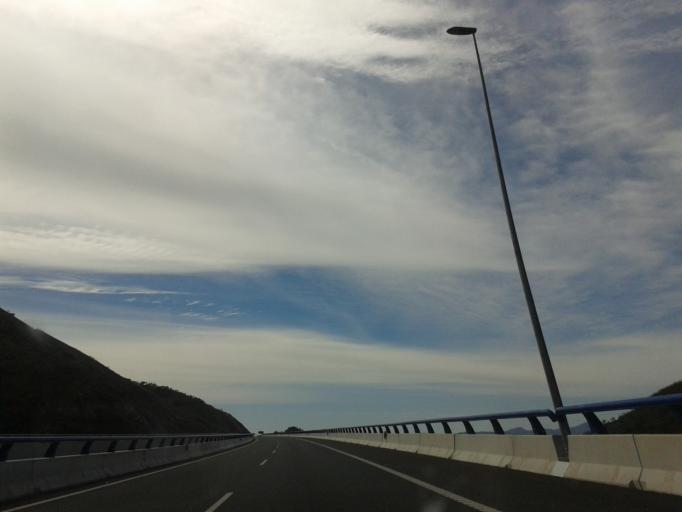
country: ES
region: Andalusia
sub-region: Provincia de Malaga
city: Almogia
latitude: 36.8553
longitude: -4.4851
